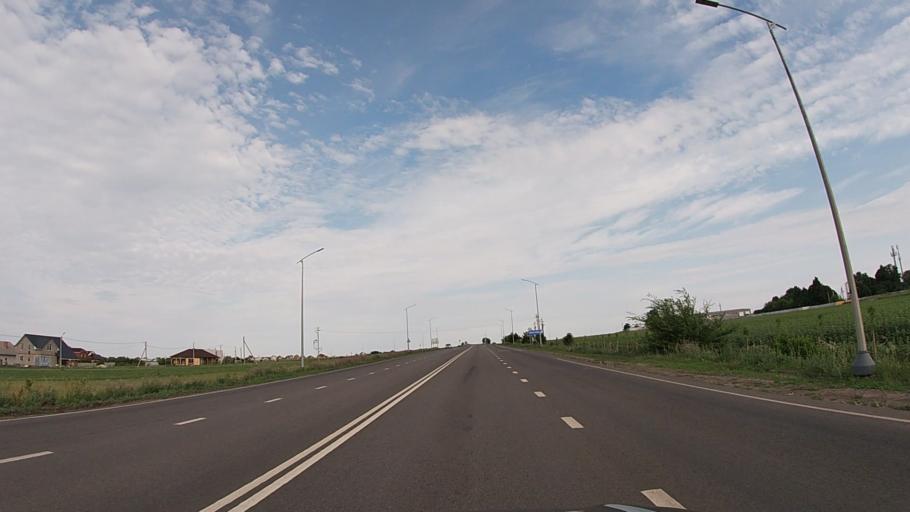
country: RU
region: Belgorod
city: Severnyy
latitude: 50.6723
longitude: 36.4798
